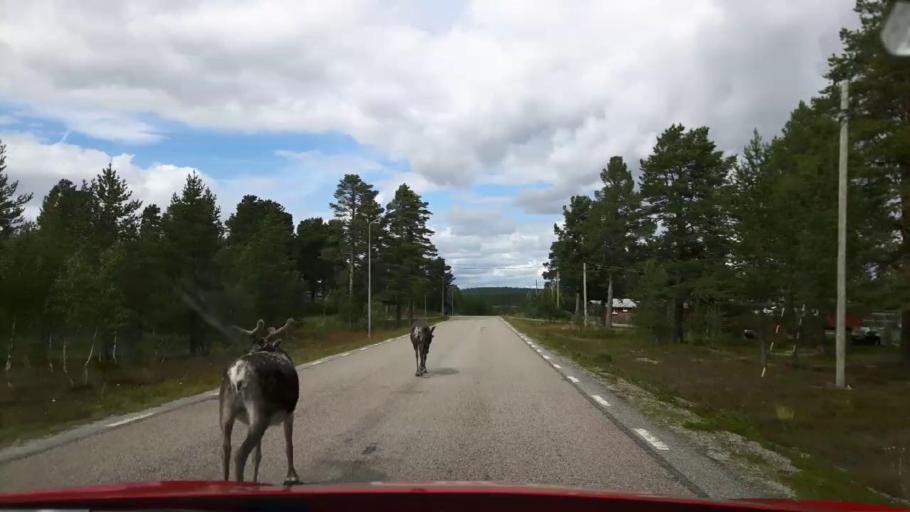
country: NO
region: Hedmark
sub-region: Engerdal
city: Engerdal
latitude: 62.3008
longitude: 12.8023
